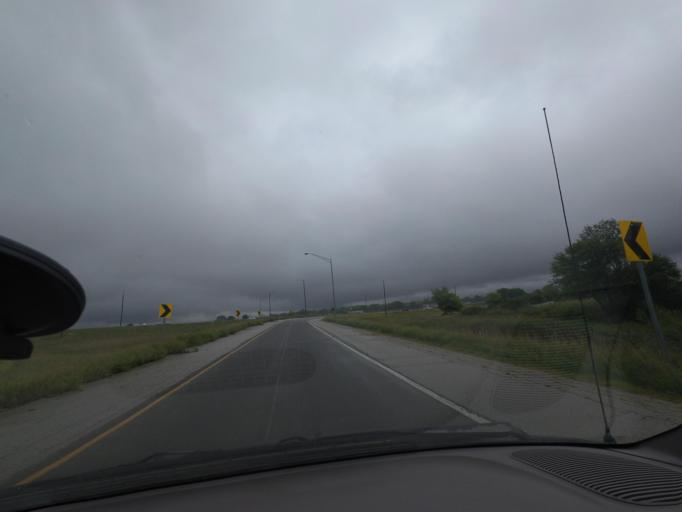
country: US
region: Illinois
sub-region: Champaign County
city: Champaign
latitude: 40.1441
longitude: -88.2834
